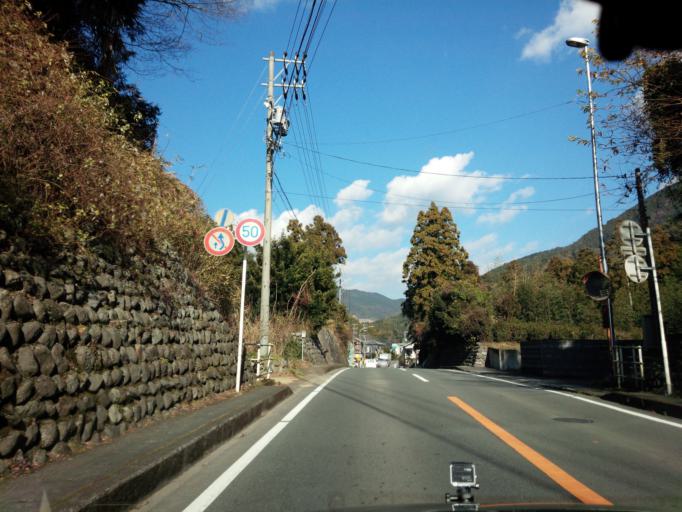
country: JP
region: Shizuoka
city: Fujinomiya
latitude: 35.1058
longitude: 138.5132
